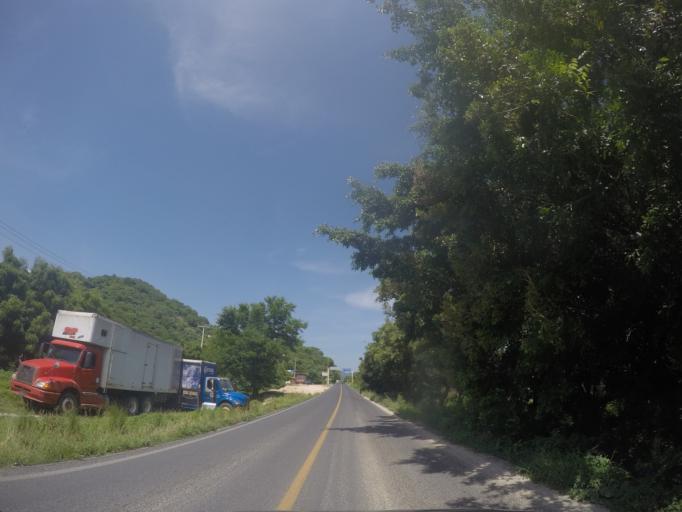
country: MX
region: Oaxaca
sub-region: Villa de Tututepec de Melchor Ocampo
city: Santa Rosa de Lima
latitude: 16.0105
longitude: -97.4500
